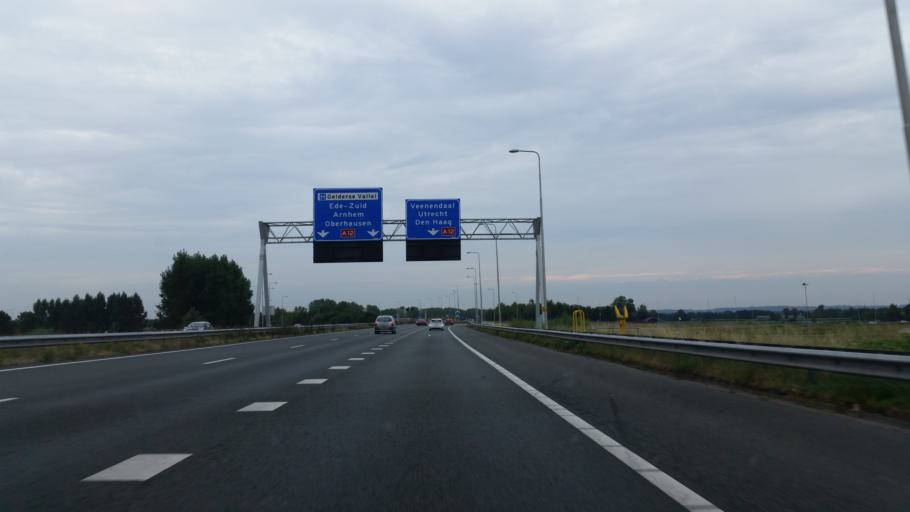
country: NL
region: Gelderland
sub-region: Gemeente Ede
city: Ede
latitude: 52.0310
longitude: 5.6132
